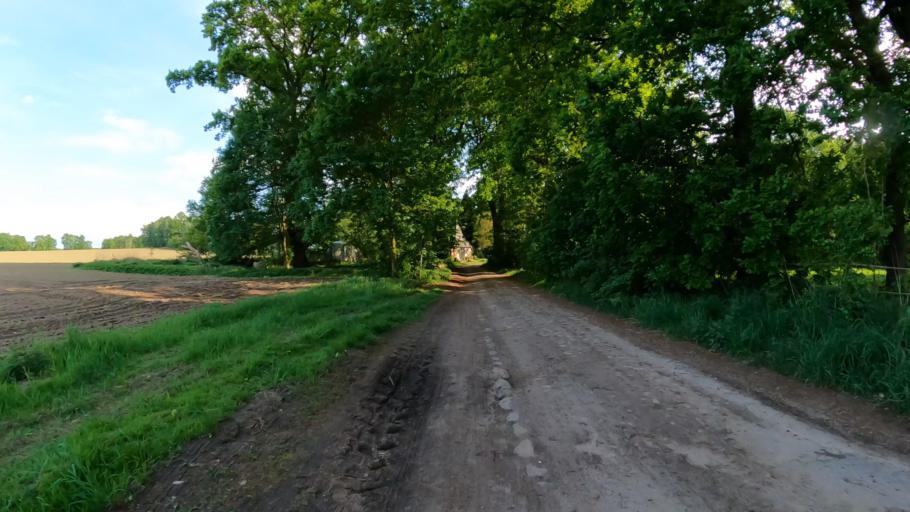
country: DE
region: Lower Saxony
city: Buchholz in der Nordheide
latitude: 53.3513
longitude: 9.9082
